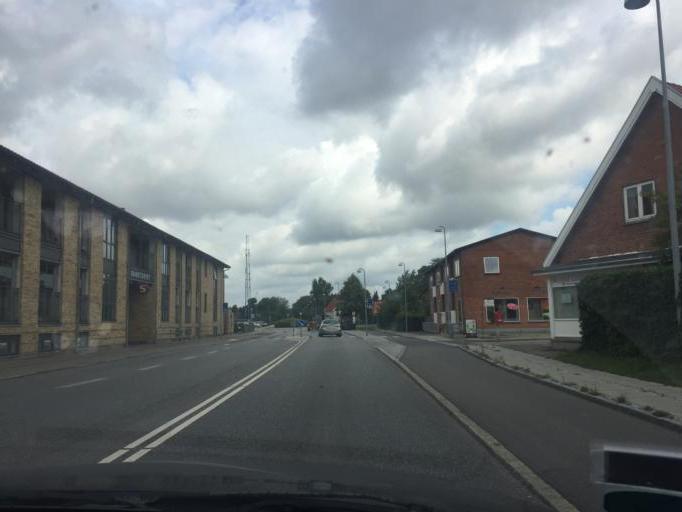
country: DK
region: Capital Region
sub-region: Allerod Kommune
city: Lillerod
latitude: 55.8710
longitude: 12.3581
